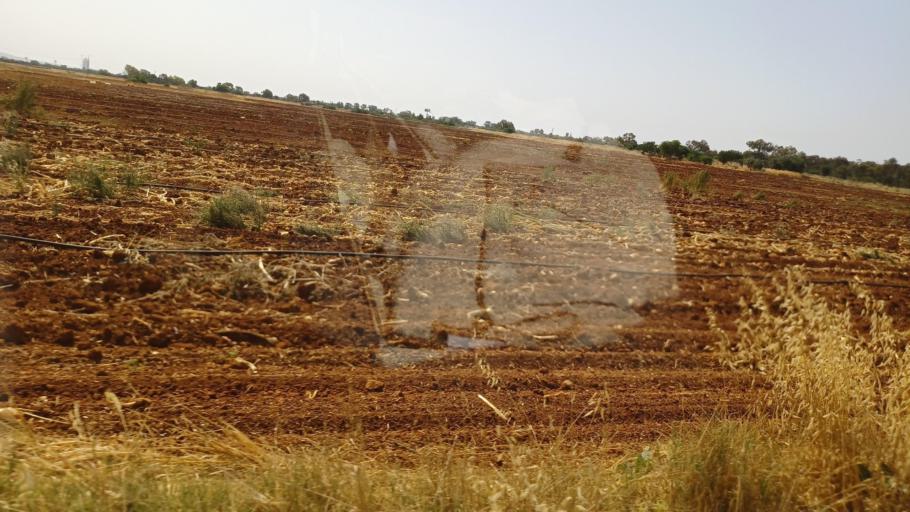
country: CY
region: Ammochostos
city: Liopetri
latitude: 34.9812
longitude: 33.8815
